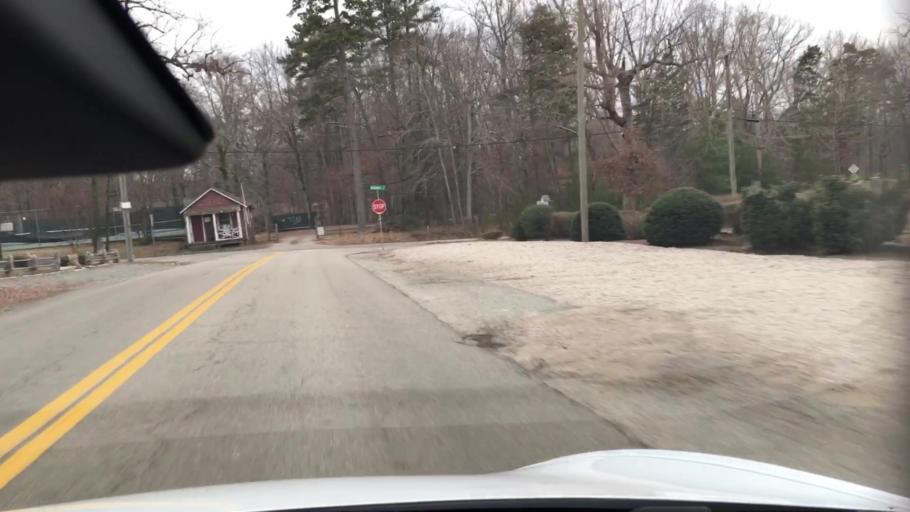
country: US
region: Virginia
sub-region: Chesterfield County
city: Bon Air
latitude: 37.5251
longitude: -77.5595
